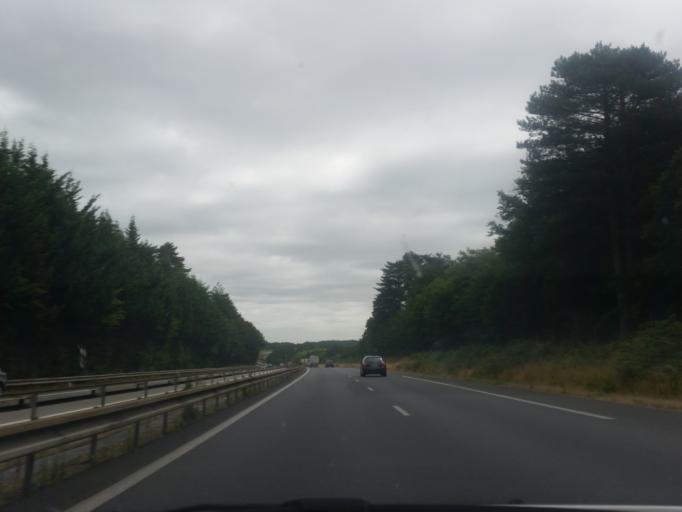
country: FR
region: Pays de la Loire
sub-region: Departement de la Loire-Atlantique
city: Carquefou
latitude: 47.2915
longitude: -1.4651
